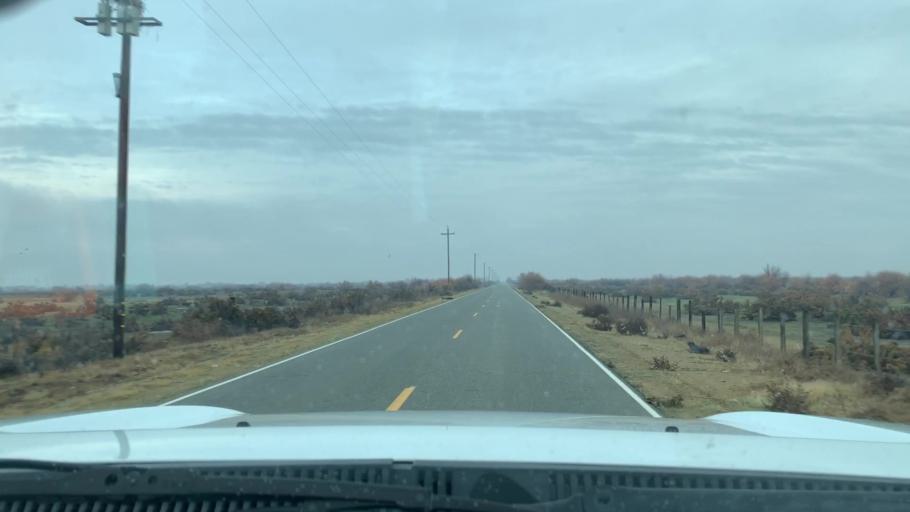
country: US
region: California
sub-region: Kern County
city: Lost Hills
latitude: 35.7040
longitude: -119.5796
